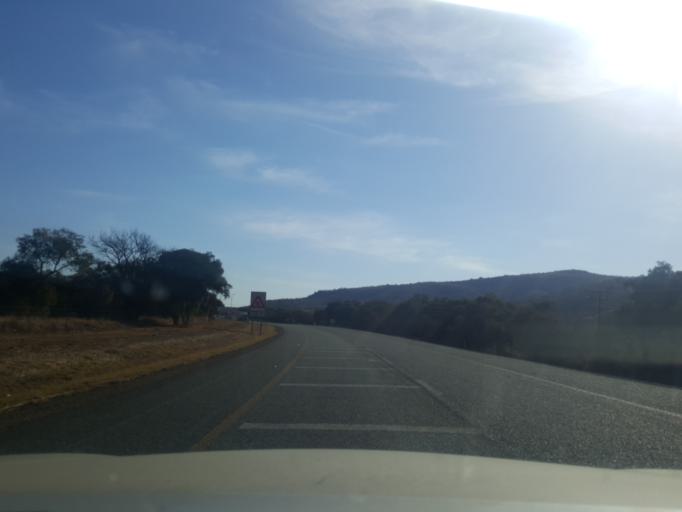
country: ZA
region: North-West
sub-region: Ngaka Modiri Molema District Municipality
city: Zeerust
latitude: -25.5417
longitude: 26.1117
